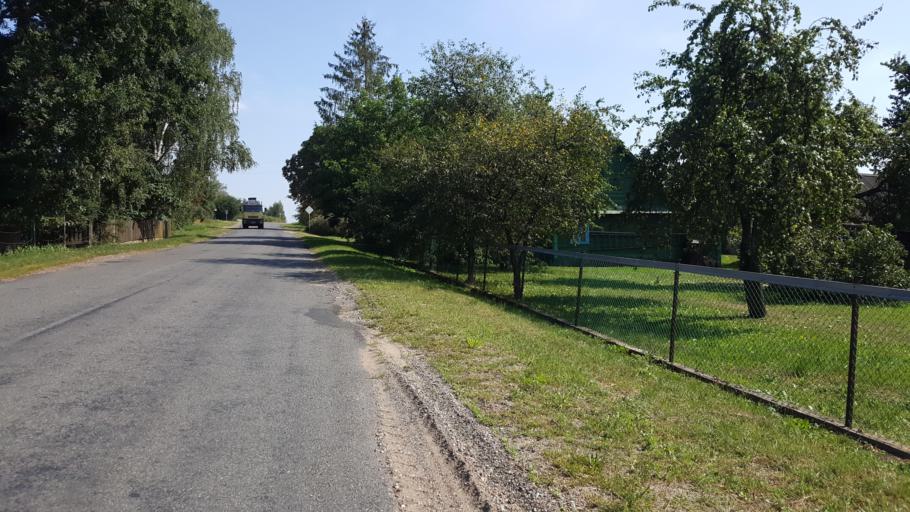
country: BY
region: Brest
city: Kamyanyets
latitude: 52.4670
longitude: 23.7140
